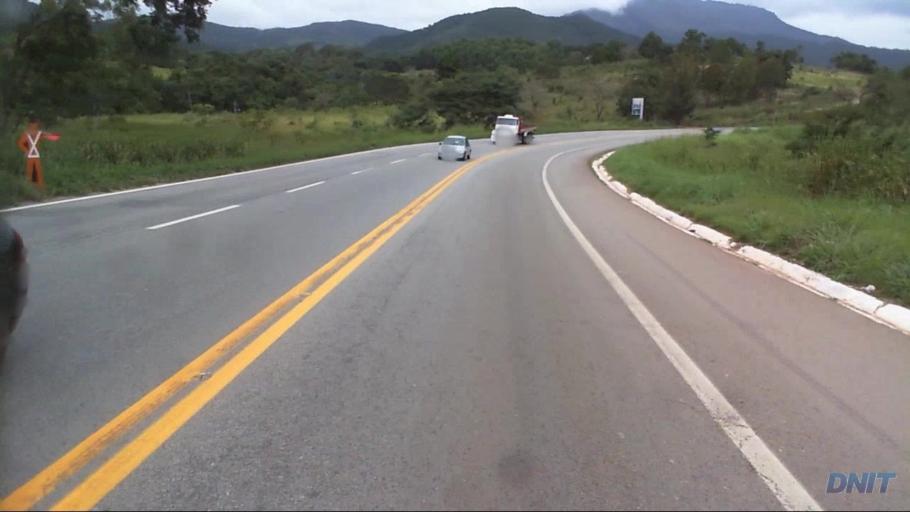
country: BR
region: Minas Gerais
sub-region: Caete
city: Caete
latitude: -19.7788
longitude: -43.6568
